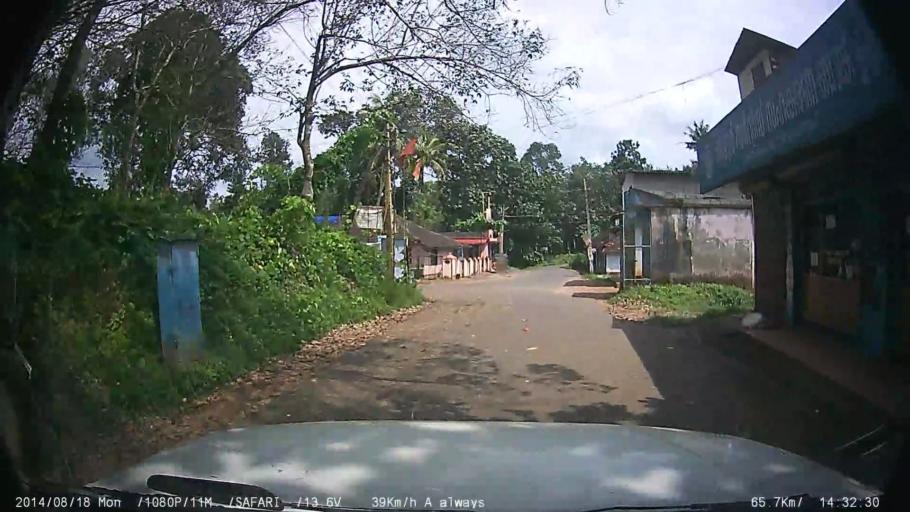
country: IN
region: Kerala
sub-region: Kottayam
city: Palackattumala
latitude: 9.7848
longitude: 76.5620
